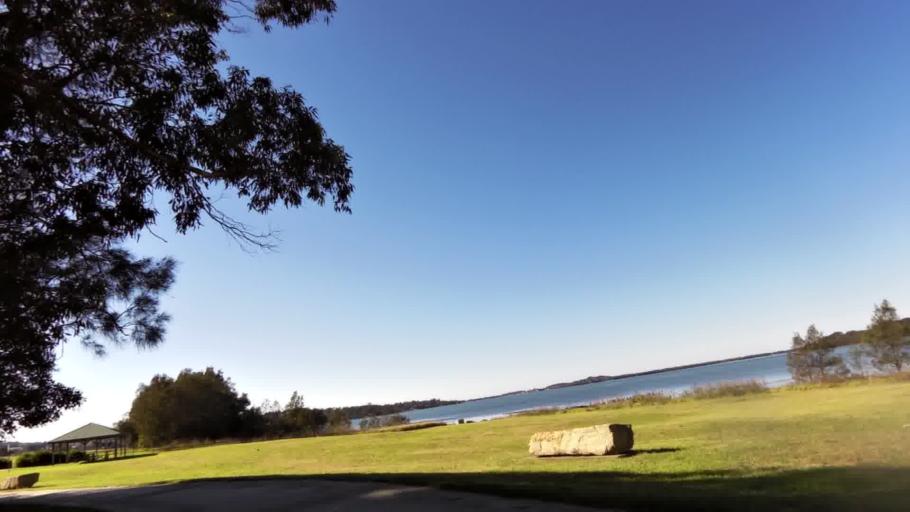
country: AU
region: New South Wales
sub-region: Wollongong
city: Berkeley
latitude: -34.4867
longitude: 150.8399
